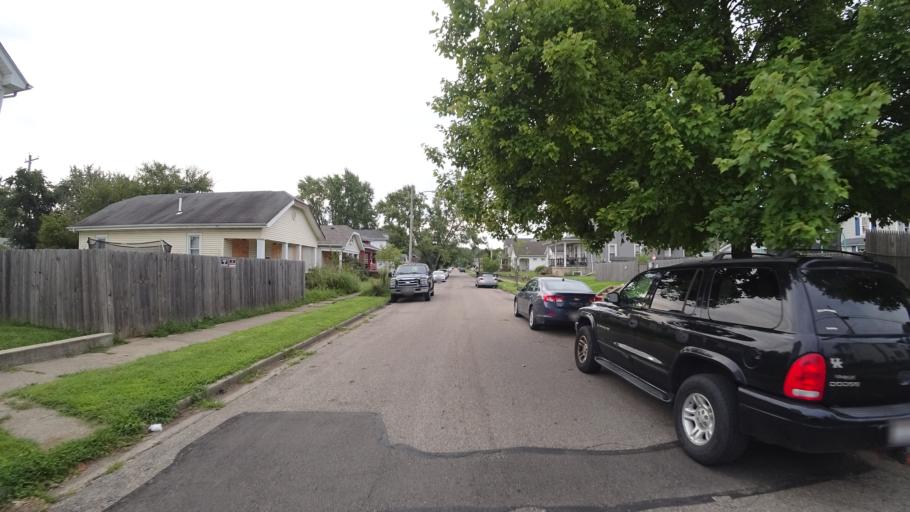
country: US
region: Ohio
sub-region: Butler County
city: Hamilton
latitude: 39.3964
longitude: -84.5458
